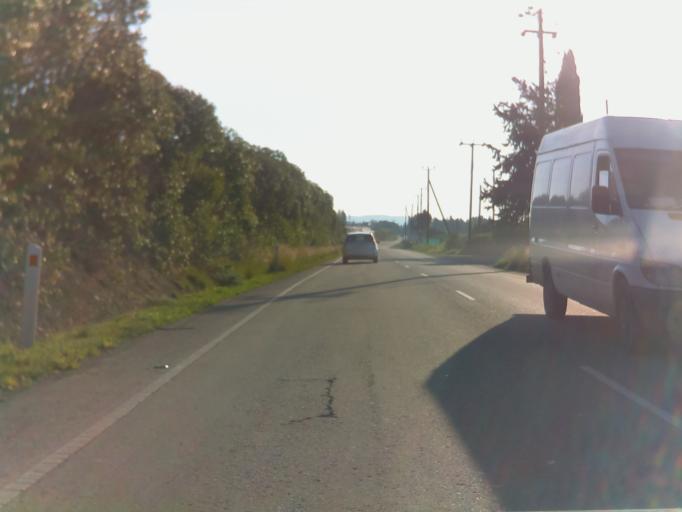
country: CY
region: Pafos
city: Paphos
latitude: 34.7333
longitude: 32.5001
